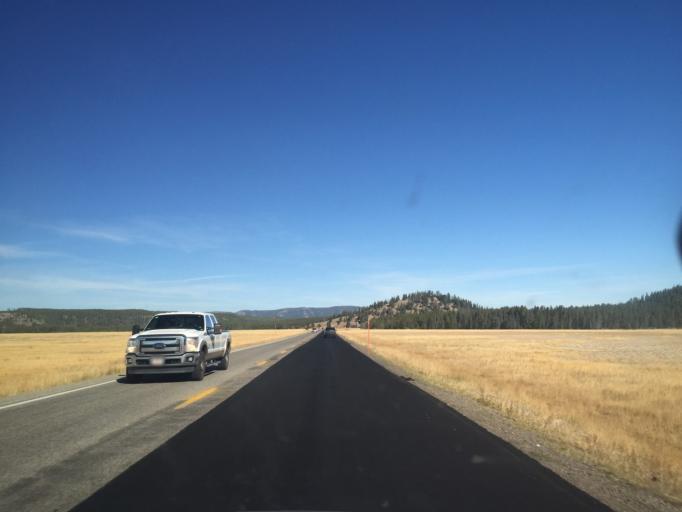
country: US
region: Montana
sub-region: Gallatin County
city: West Yellowstone
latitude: 44.5608
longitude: -110.8103
